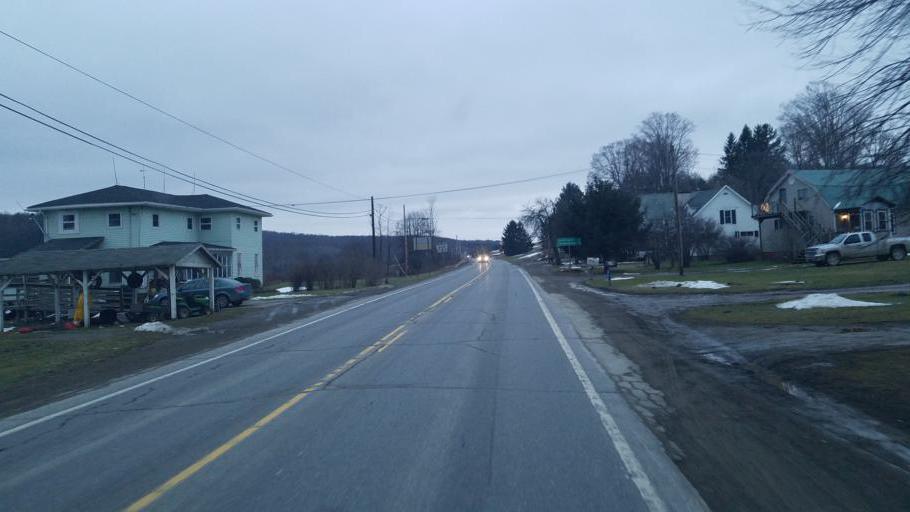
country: US
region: Pennsylvania
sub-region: Potter County
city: Coudersport
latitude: 41.8717
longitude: -77.8382
